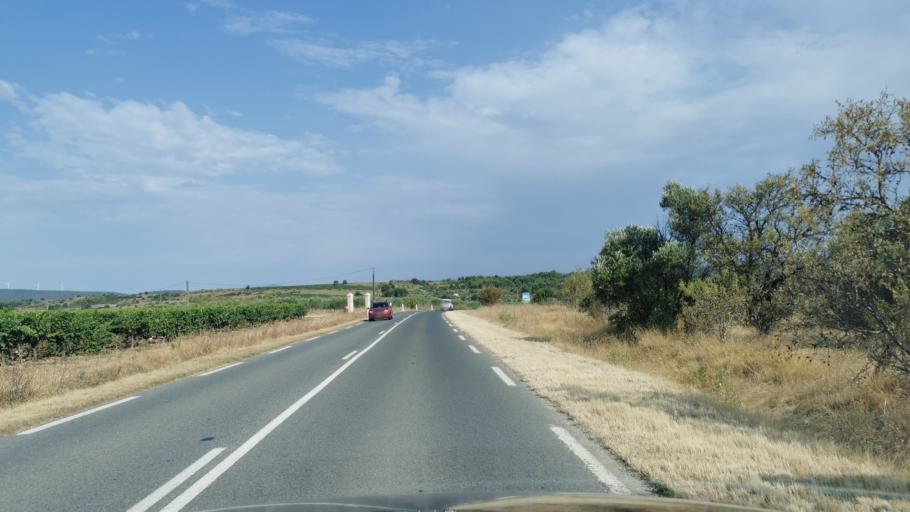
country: FR
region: Languedoc-Roussillon
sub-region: Departement de l'Aude
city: Ginestas
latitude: 43.2855
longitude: 2.8723
